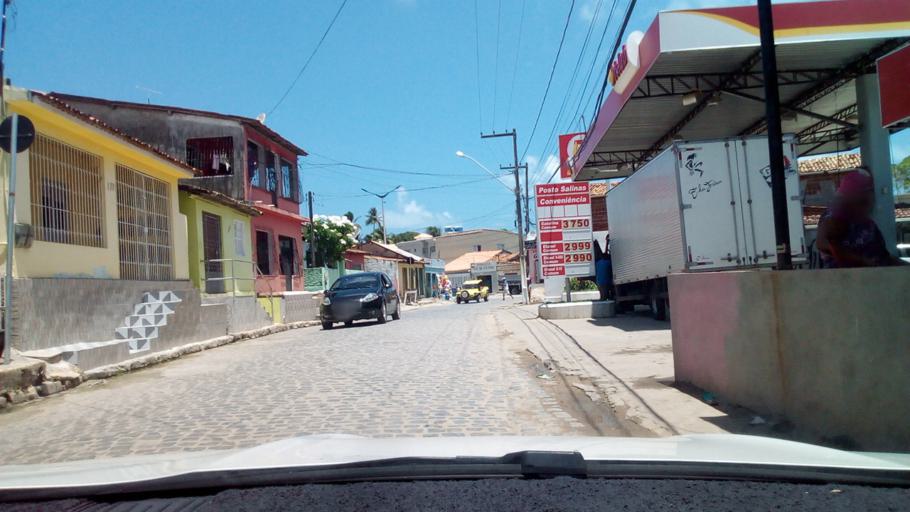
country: BR
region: Paraiba
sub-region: Pitimbu
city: Pitimbu
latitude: -7.4751
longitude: -34.8109
